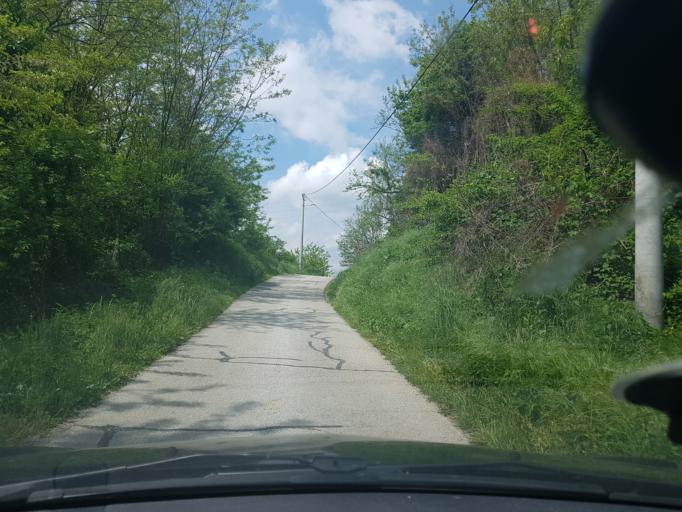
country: SI
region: Rogatec
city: Rogatec
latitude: 46.2135
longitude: 15.7169
